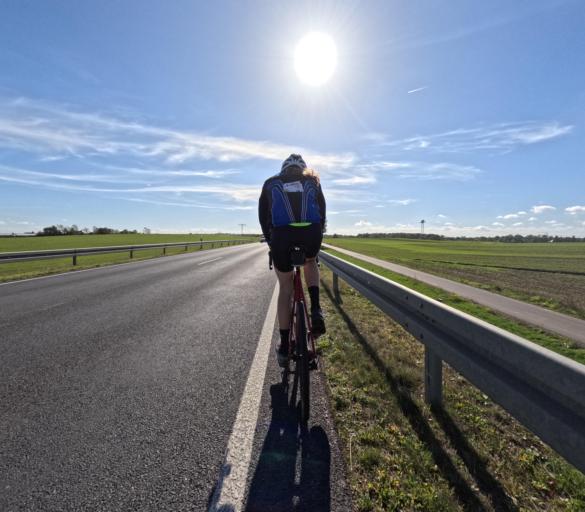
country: DE
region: Saxony
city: Moritzburg
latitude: 51.1424
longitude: 13.6514
